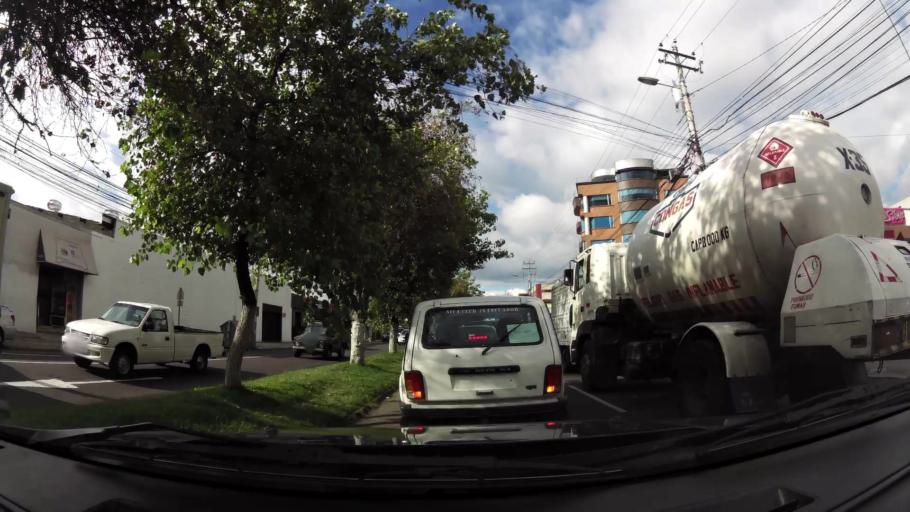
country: EC
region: Pichincha
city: Quito
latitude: -0.1559
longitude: -78.4791
